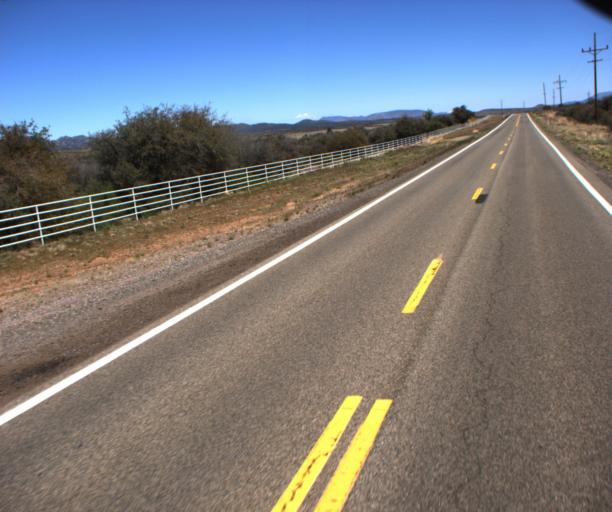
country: US
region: Arizona
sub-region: Yavapai County
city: Congress
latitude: 34.2484
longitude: -112.7359
